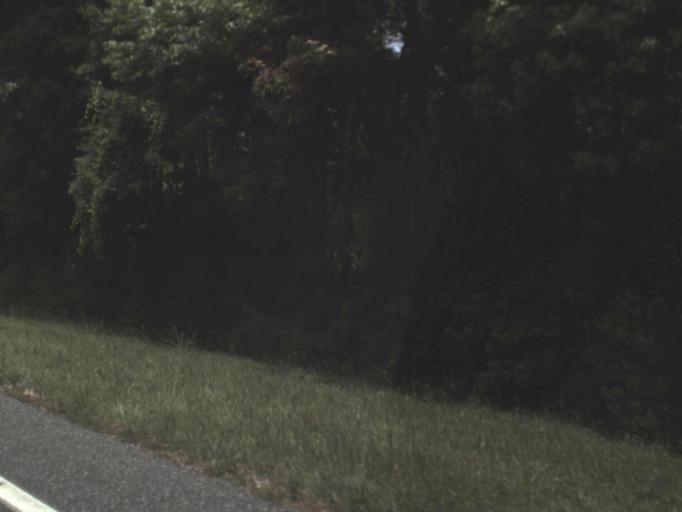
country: US
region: Florida
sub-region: Taylor County
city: Perry
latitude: 29.9314
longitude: -83.4445
